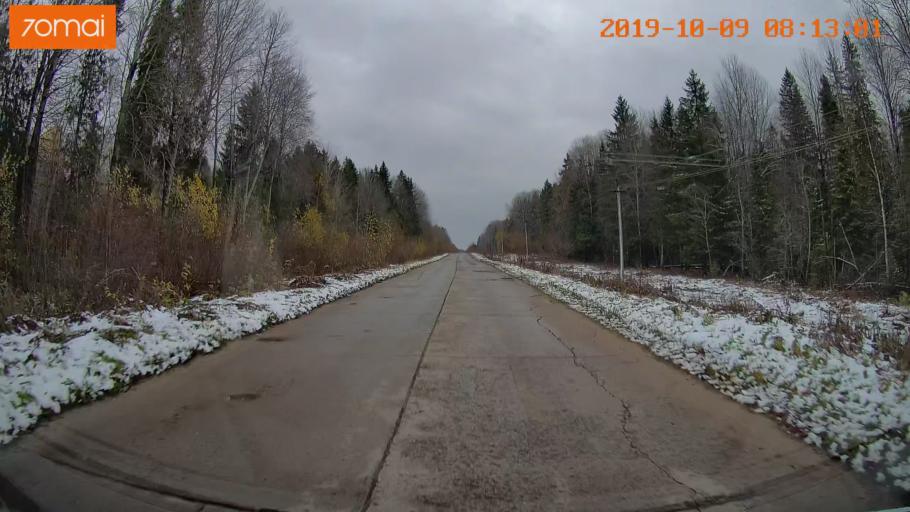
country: RU
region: Vologda
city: Gryazovets
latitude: 58.7214
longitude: 40.1334
